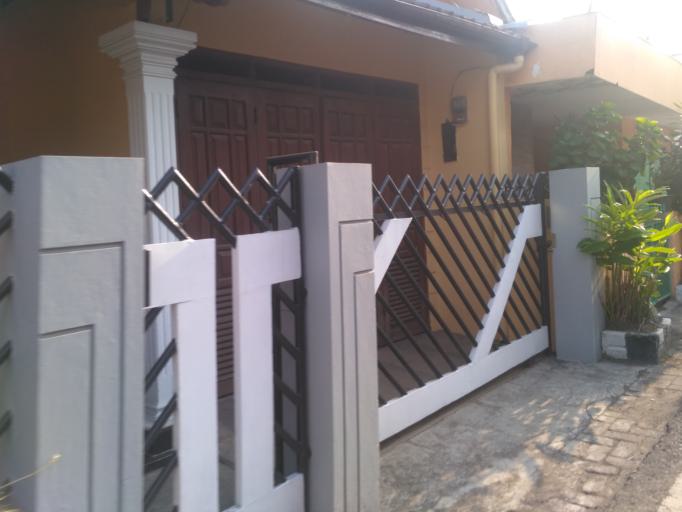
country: ID
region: East Java
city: Malang
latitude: -7.9583
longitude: 112.6270
